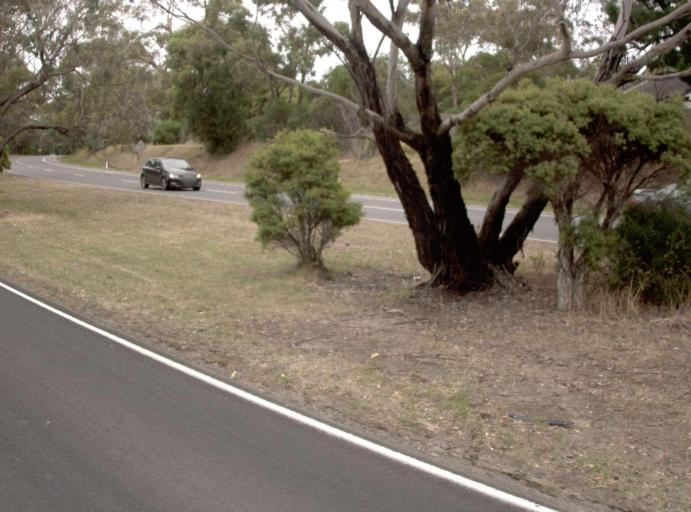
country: AU
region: Victoria
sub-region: Mornington Peninsula
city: Mount Eliza
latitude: -38.1926
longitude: 145.0944
